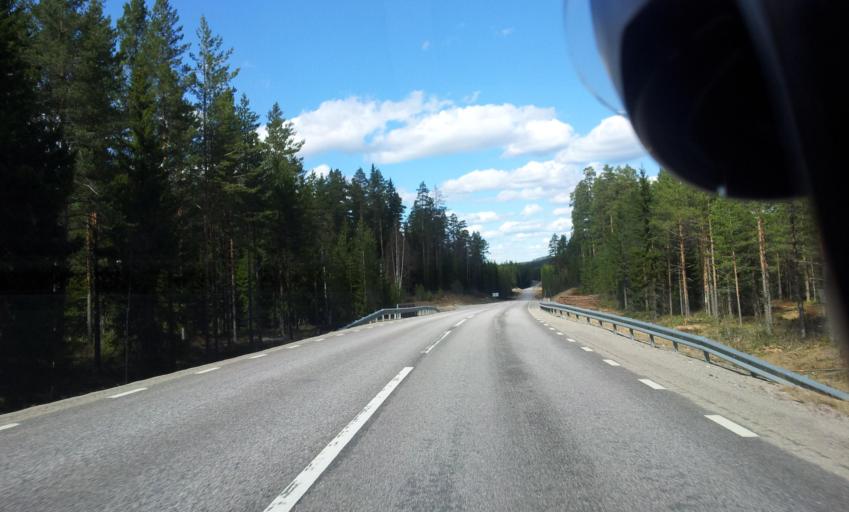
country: SE
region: Gaevleborg
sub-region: Bollnas Kommun
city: Vittsjo
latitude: 61.1594
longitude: 15.8818
